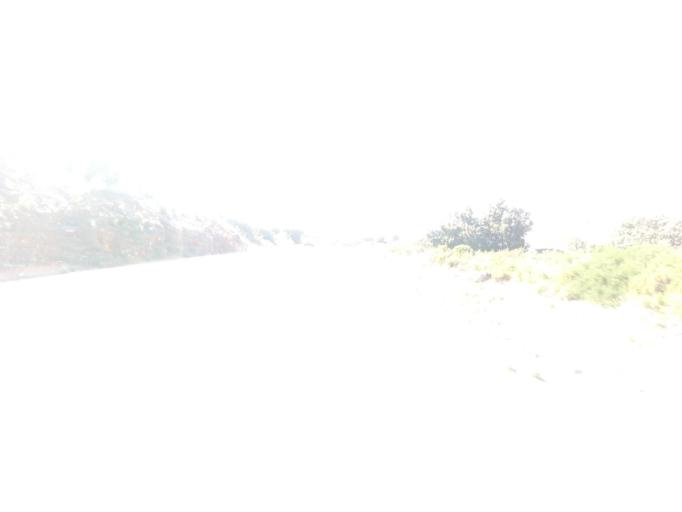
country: ES
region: Valencia
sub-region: Provincia de Castello
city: Sierra-Engarceran
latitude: 40.3140
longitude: -0.0327
